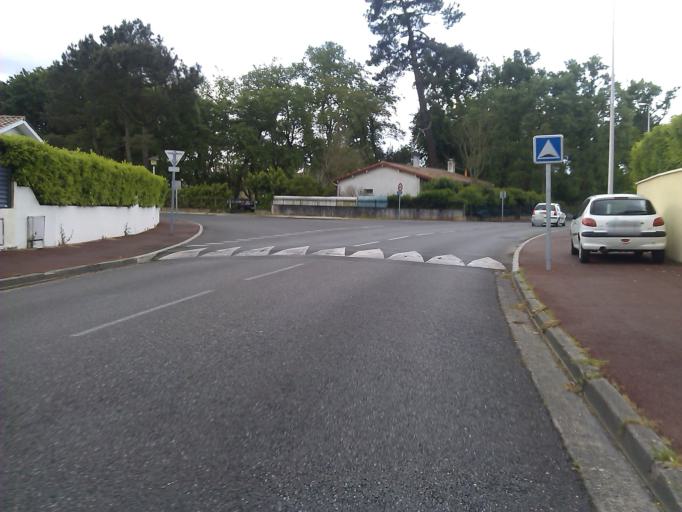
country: FR
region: Aquitaine
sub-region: Departement de la Gironde
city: Cestas
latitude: 44.7441
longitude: -0.6848
